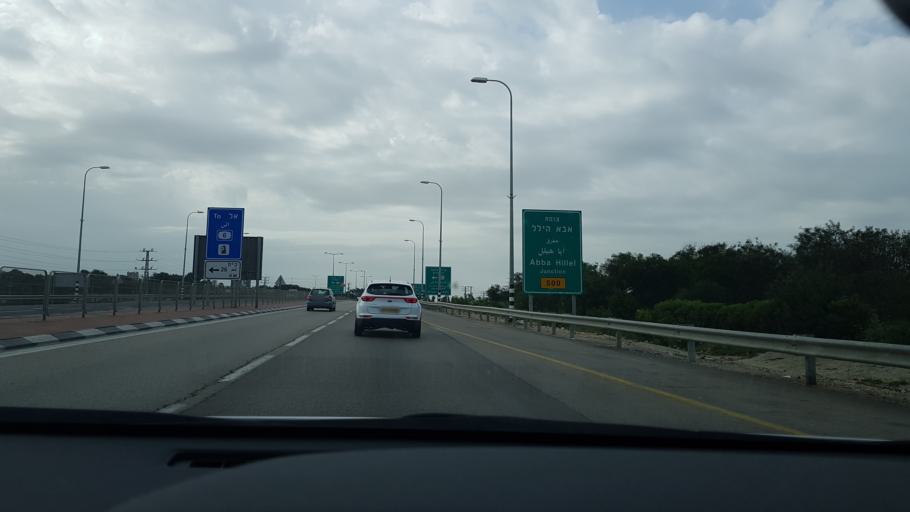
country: IL
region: Southern District
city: Ashqelon
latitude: 31.6795
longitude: 34.6097
